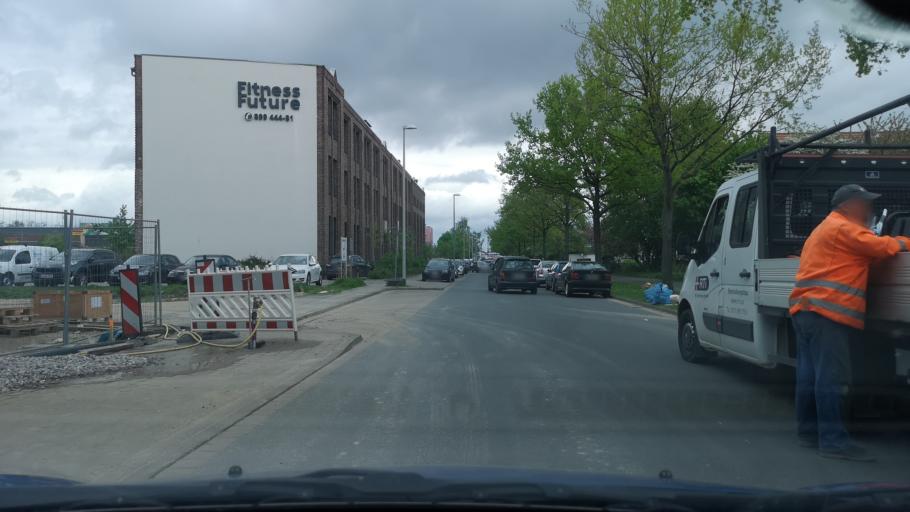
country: DE
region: Lower Saxony
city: Hannover
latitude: 52.4044
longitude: 9.7143
